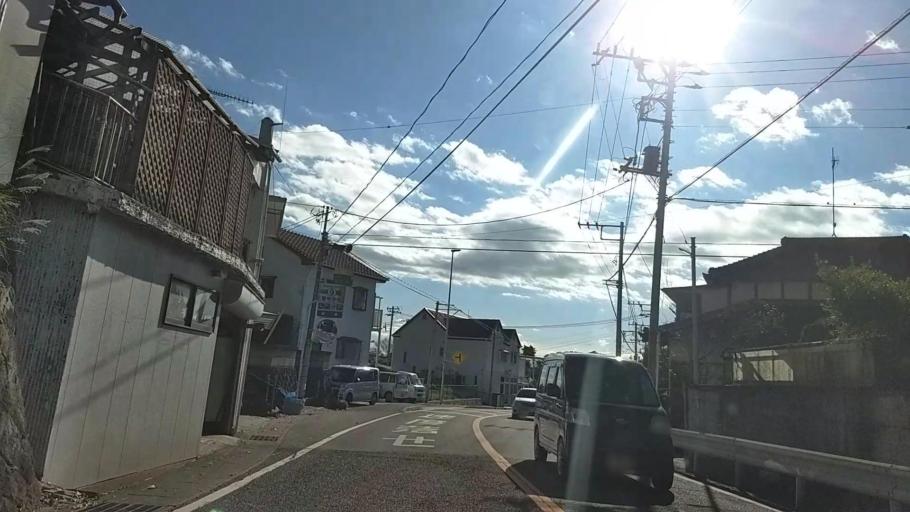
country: JP
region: Chiba
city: Tateyama
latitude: 35.0490
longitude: 139.8343
